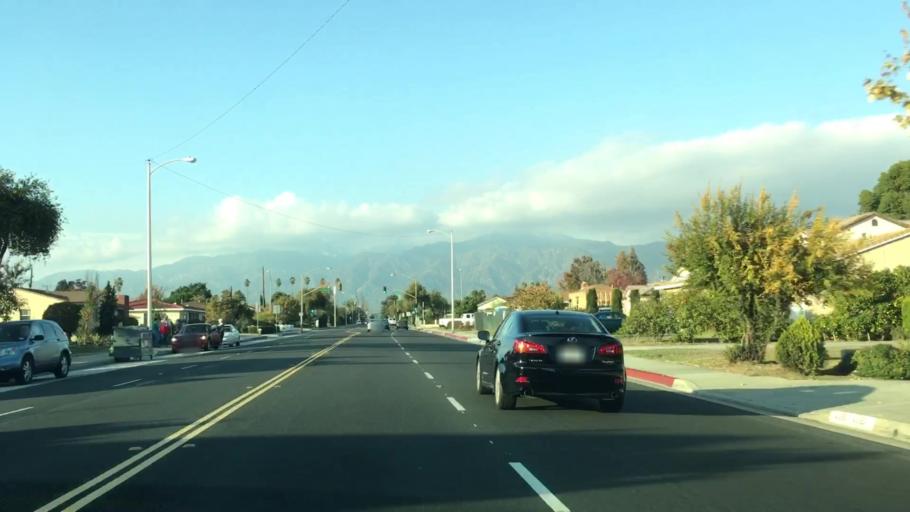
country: US
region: California
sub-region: Los Angeles County
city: Temple City
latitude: 34.0924
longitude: -118.0579
